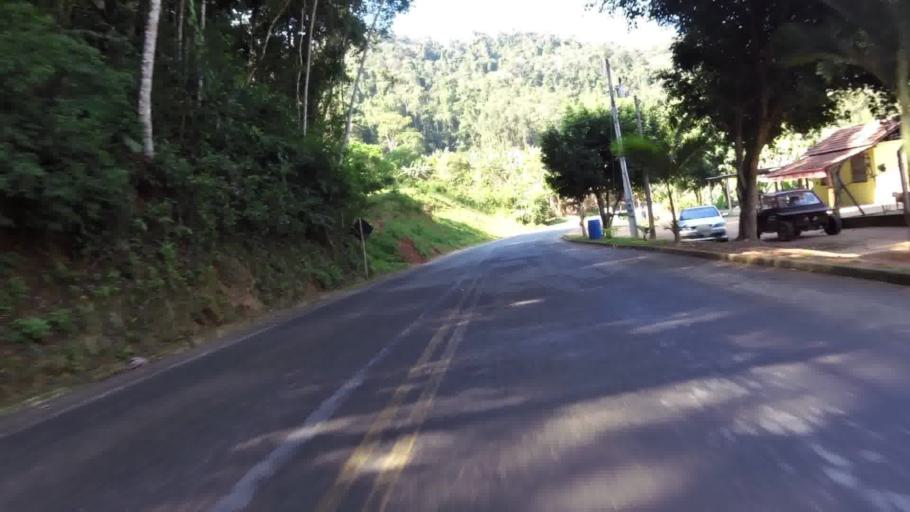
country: BR
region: Espirito Santo
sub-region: Alfredo Chaves
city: Alfredo Chaves
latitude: -20.5765
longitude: -40.8000
